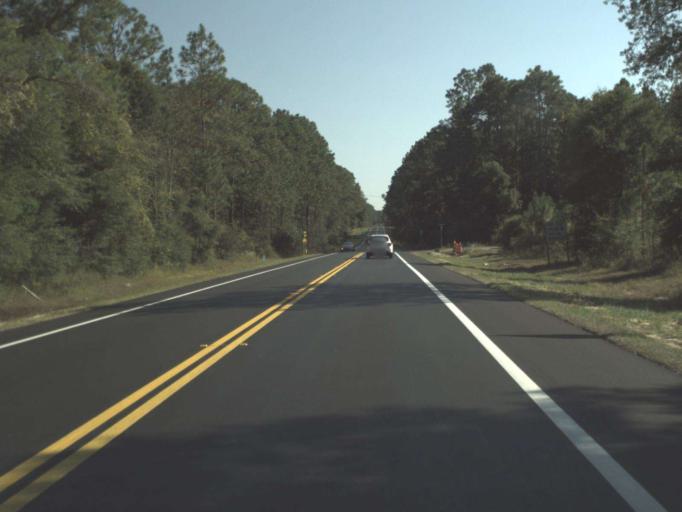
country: US
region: Florida
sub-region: Walton County
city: DeFuniak Springs
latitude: 30.7622
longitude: -86.1529
